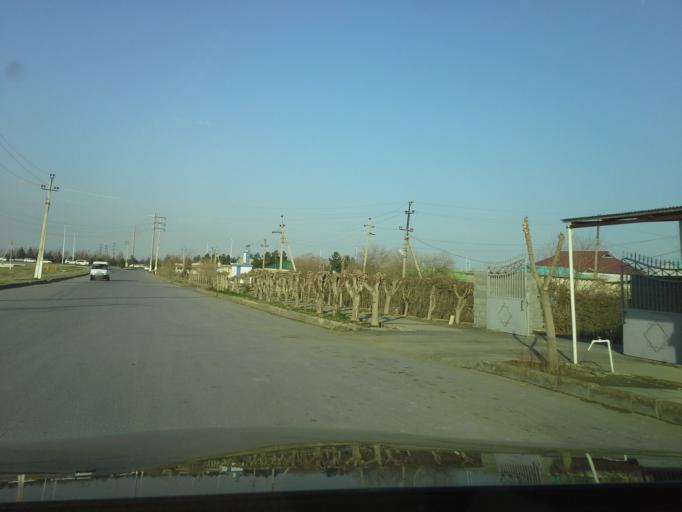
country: TM
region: Ahal
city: Abadan
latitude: 38.0303
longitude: 58.2253
